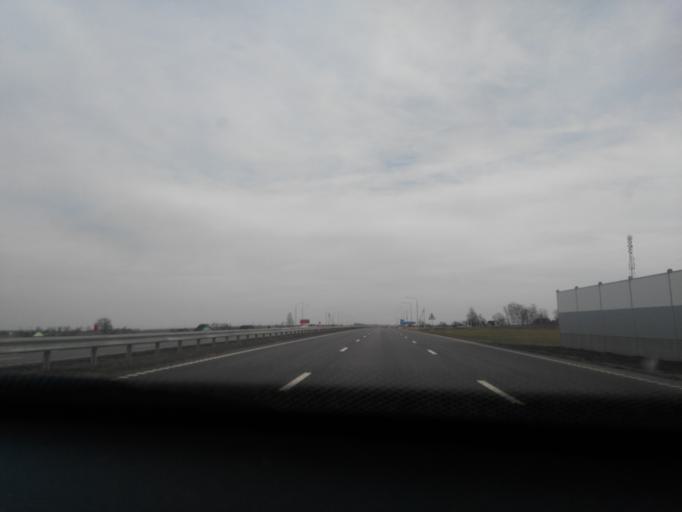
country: BY
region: Gomel
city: Zhlobin
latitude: 52.9811
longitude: 29.8306
